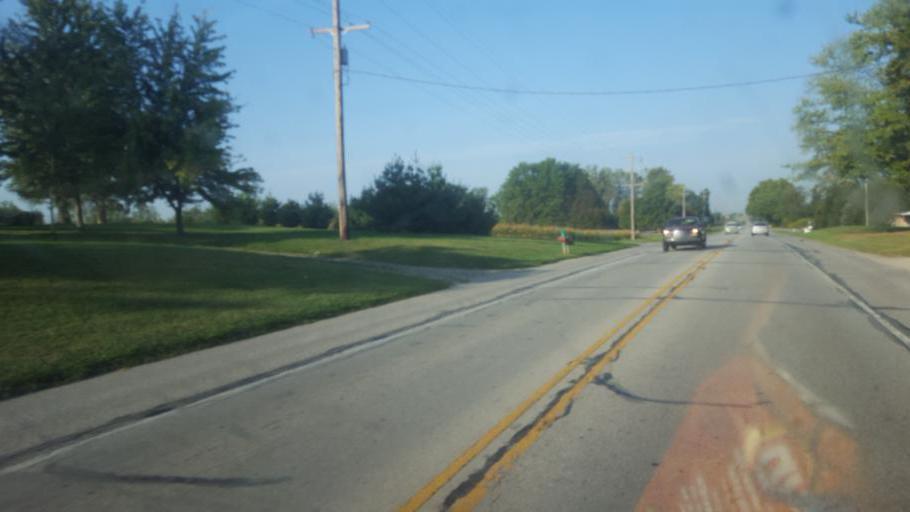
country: US
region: Indiana
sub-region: LaGrange County
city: Lagrange
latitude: 41.6413
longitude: -85.4459
